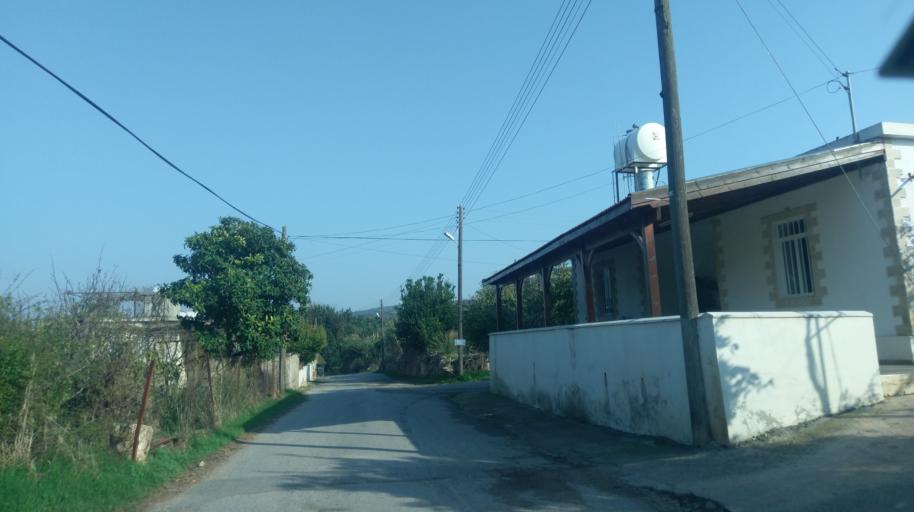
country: CY
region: Ammochostos
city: Leonarisso
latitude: 35.5421
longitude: 34.2206
